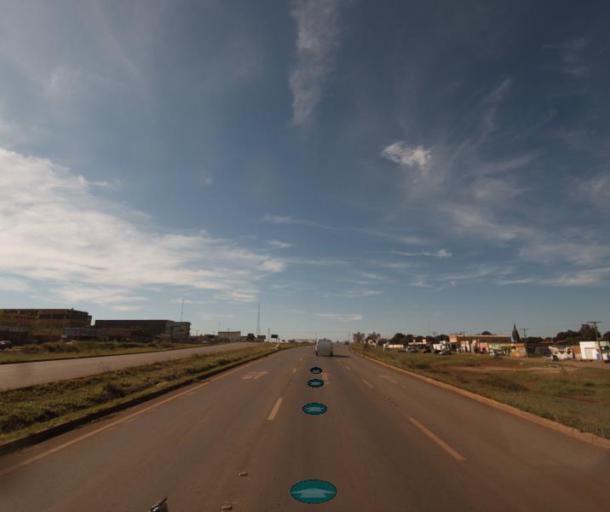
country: BR
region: Federal District
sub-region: Brasilia
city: Brasilia
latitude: -15.7474
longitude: -48.2646
